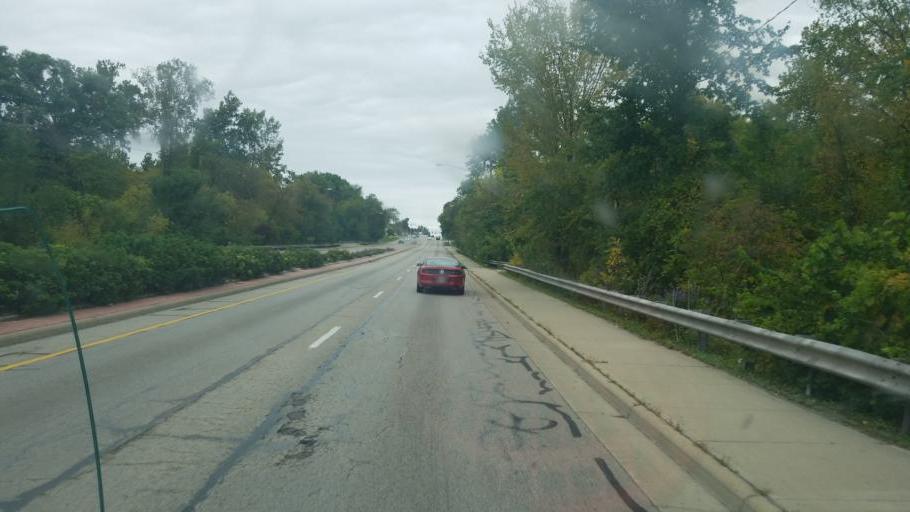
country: US
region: Ohio
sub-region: Lucas County
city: Maumee
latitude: 41.6097
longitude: -83.6646
